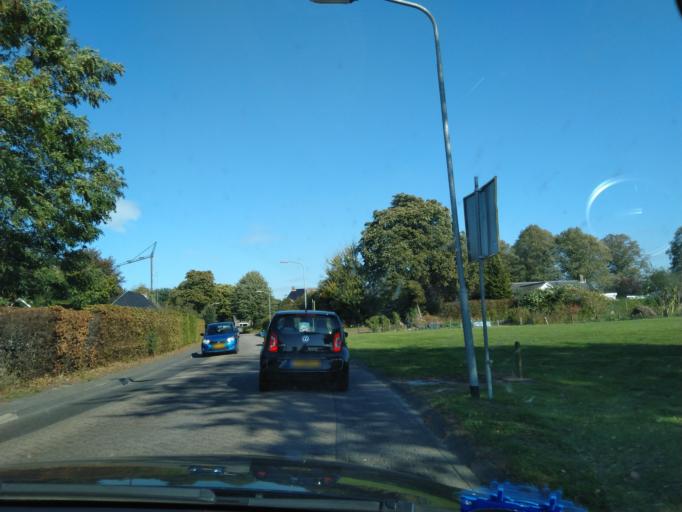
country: NL
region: Drenthe
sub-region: Gemeente Aa en Hunze
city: Anloo
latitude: 53.0522
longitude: 6.7235
